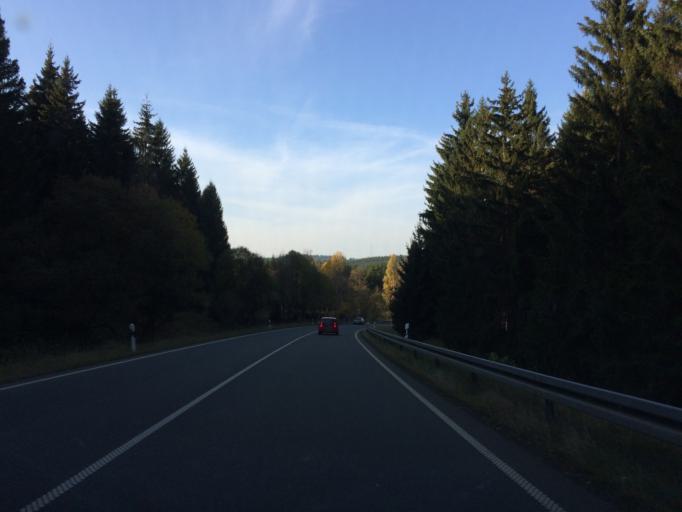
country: DE
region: Lower Saxony
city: Braunlage
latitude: 51.7091
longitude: 10.5929
